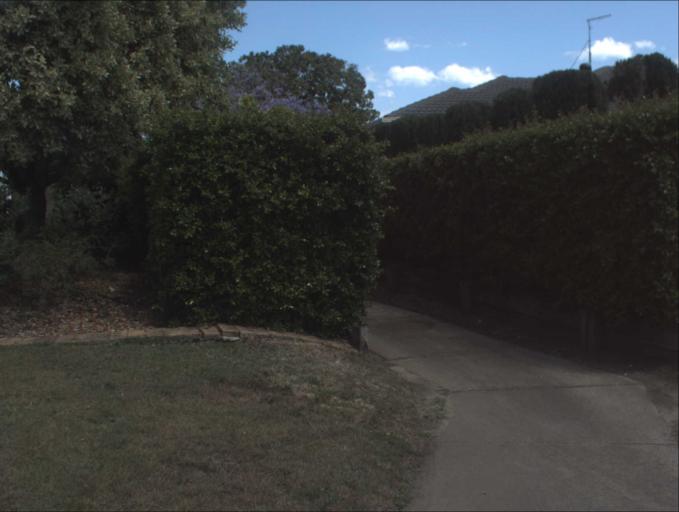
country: AU
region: Queensland
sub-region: Logan
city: Windaroo
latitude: -27.7486
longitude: 153.1956
